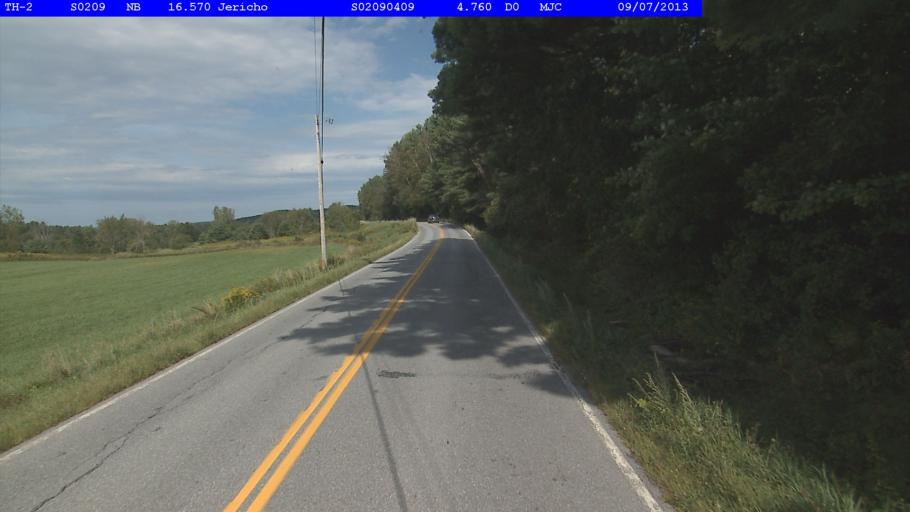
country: US
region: Vermont
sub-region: Chittenden County
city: Jericho
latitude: 44.4910
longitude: -72.9828
